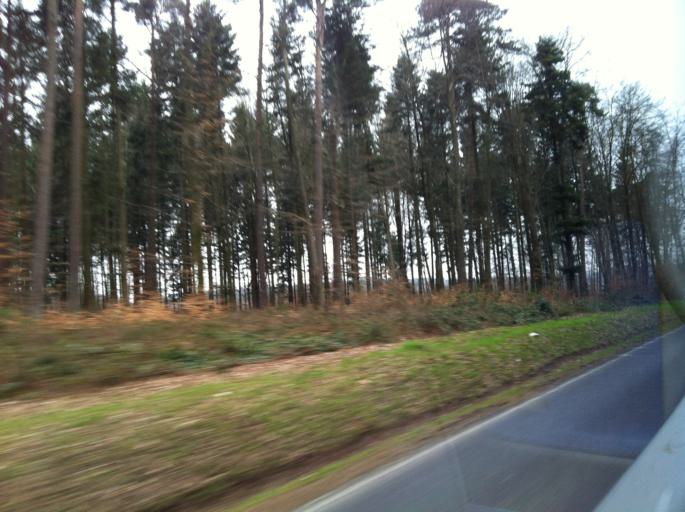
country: DE
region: Baden-Wuerttemberg
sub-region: Karlsruhe Region
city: Fahrenbach
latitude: 49.4408
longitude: 9.1545
